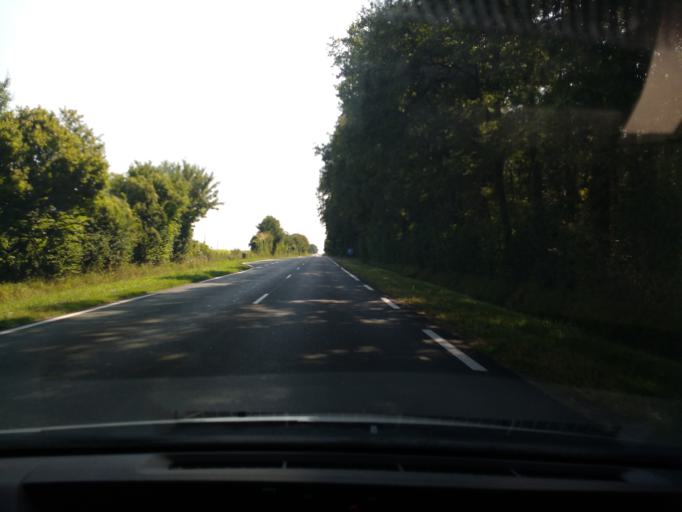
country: FR
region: Pays de la Loire
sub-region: Departement de Maine-et-Loire
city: Bauge-en-Anjou
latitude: 47.5315
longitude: -0.0522
